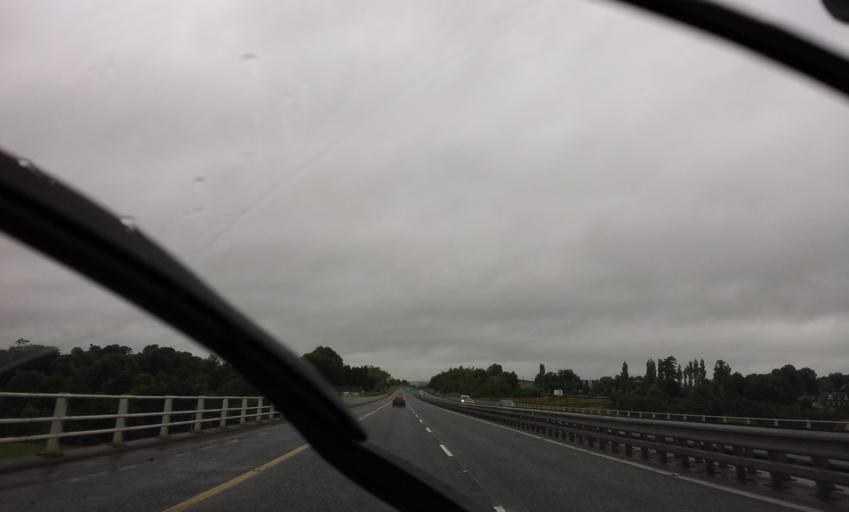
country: IE
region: Munster
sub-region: County Cork
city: Fermoy
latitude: 52.1389
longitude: -8.2617
